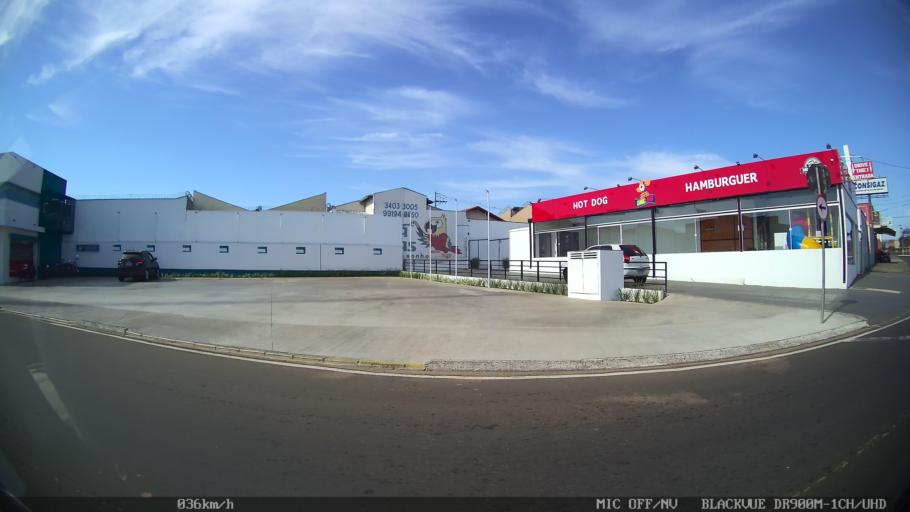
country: BR
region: Sao Paulo
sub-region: Franca
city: Franca
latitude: -20.5261
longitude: -47.4320
